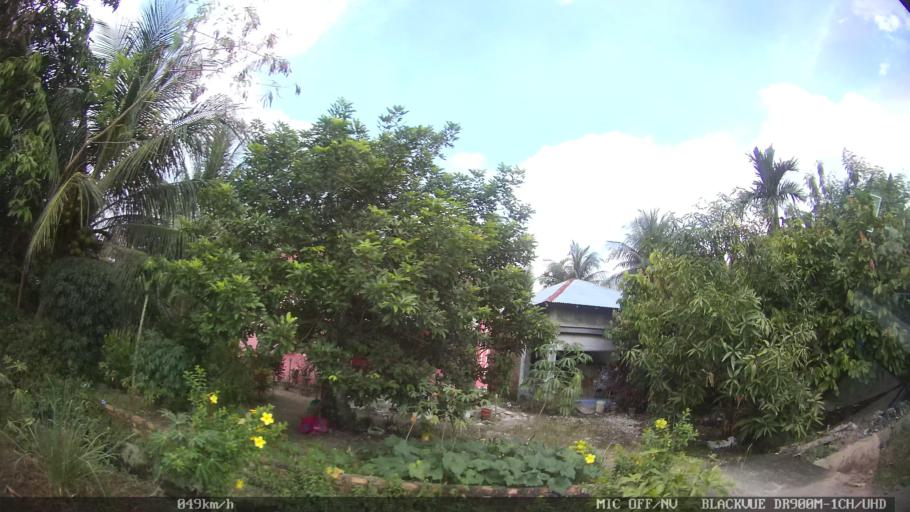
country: ID
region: North Sumatra
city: Binjai
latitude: 3.6317
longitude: 98.5024
